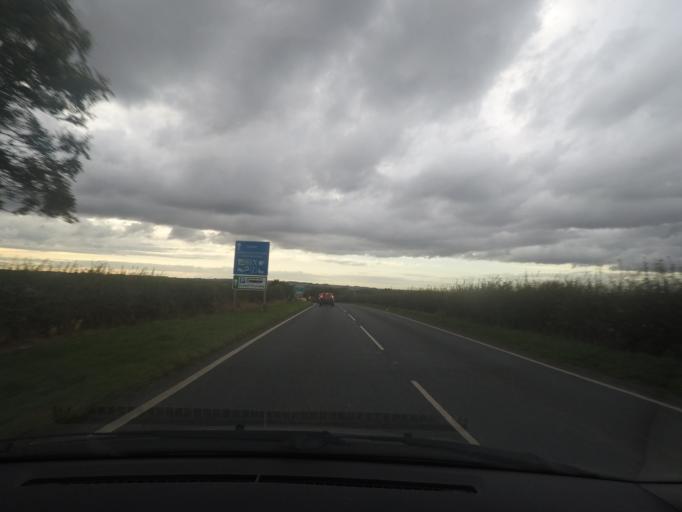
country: GB
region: England
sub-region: Lincolnshire
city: Louth
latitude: 53.3426
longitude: 0.0061
